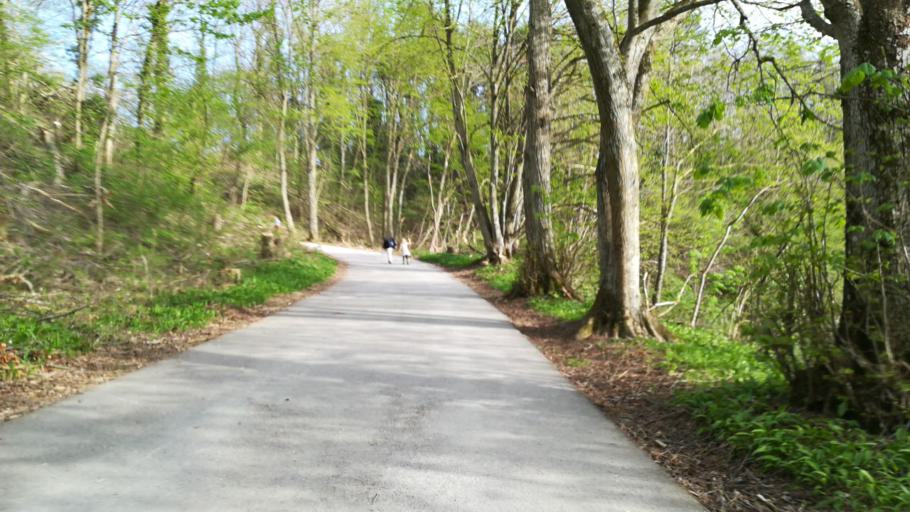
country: DE
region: Baden-Wuerttemberg
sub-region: Freiburg Region
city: Singen
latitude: 47.7648
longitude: 8.8152
